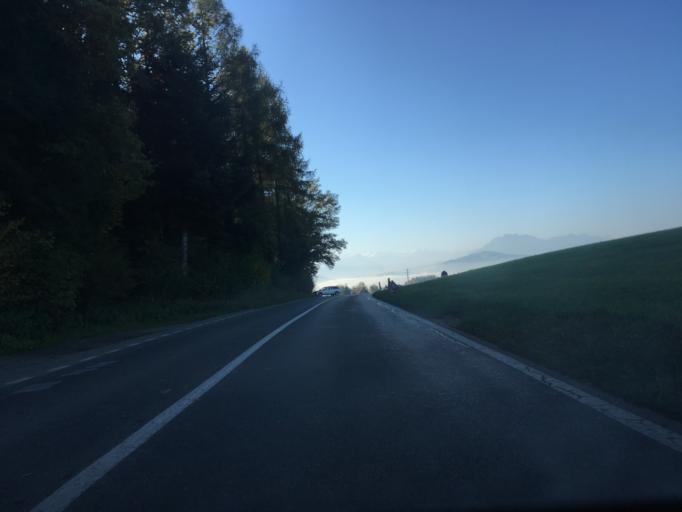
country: CH
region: Zug
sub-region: Zug
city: Baar
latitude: 47.2160
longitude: 8.5187
